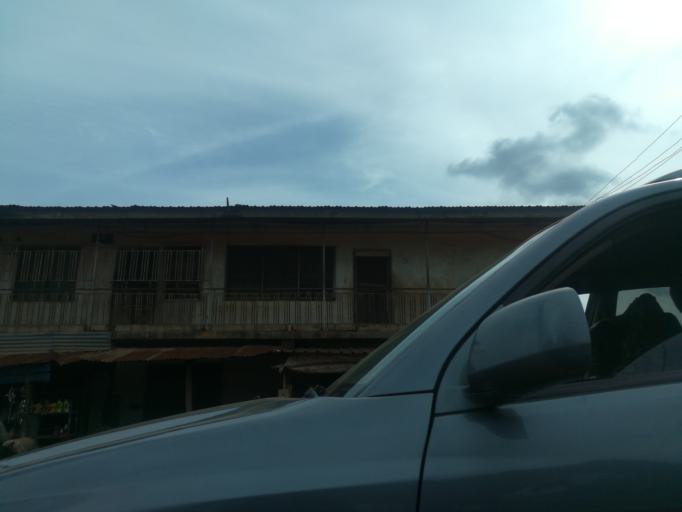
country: NG
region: Oyo
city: Ibadan
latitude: 7.3794
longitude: 3.9493
